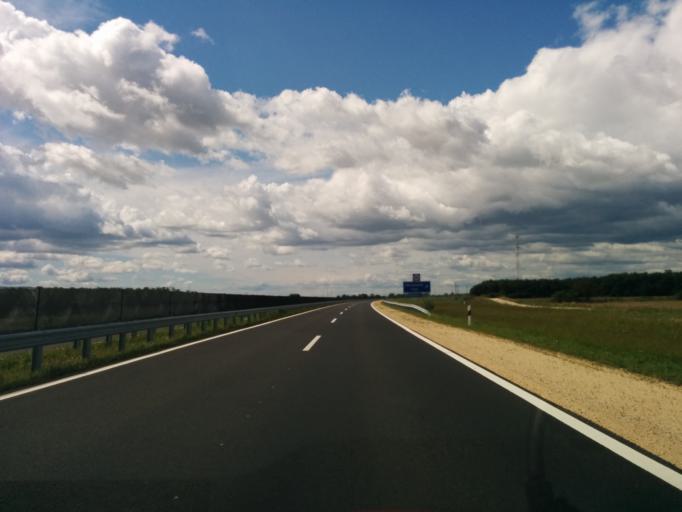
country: HU
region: Vas
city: Vep
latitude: 47.2627
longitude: 16.7389
